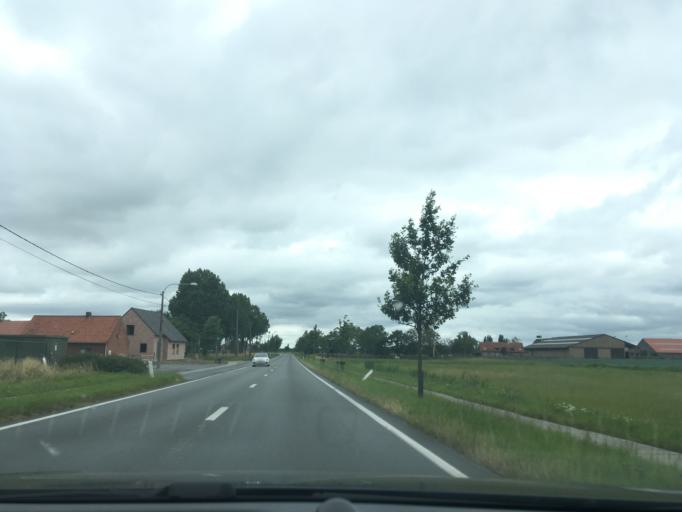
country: BE
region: Flanders
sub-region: Provincie West-Vlaanderen
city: Wingene
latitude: 51.0416
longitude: 3.3030
